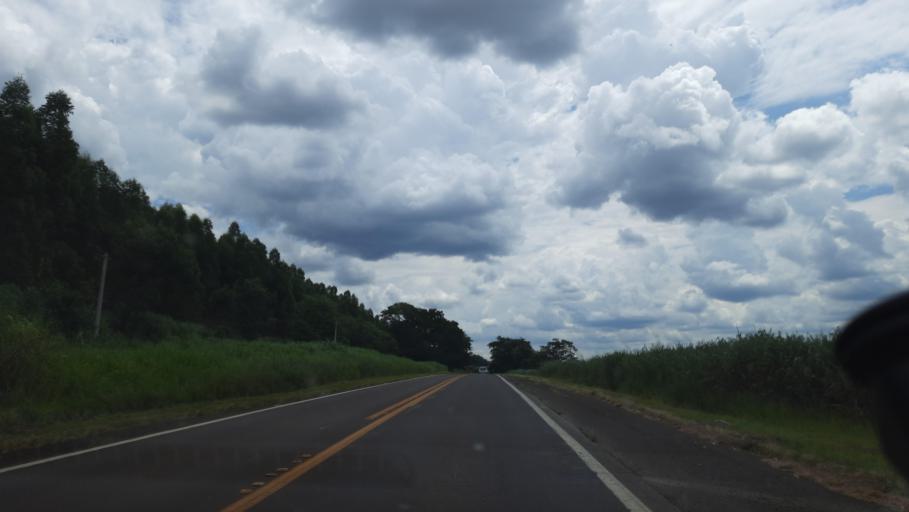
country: BR
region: Sao Paulo
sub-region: Mococa
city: Mococa
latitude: -21.4596
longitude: -47.1139
